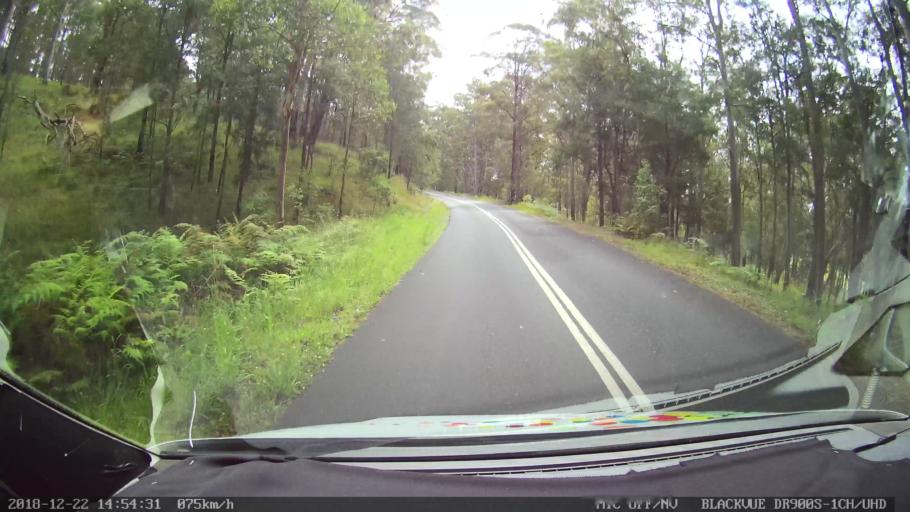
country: AU
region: New South Wales
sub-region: Bellingen
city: Dorrigo
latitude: -30.2267
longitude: 152.5318
